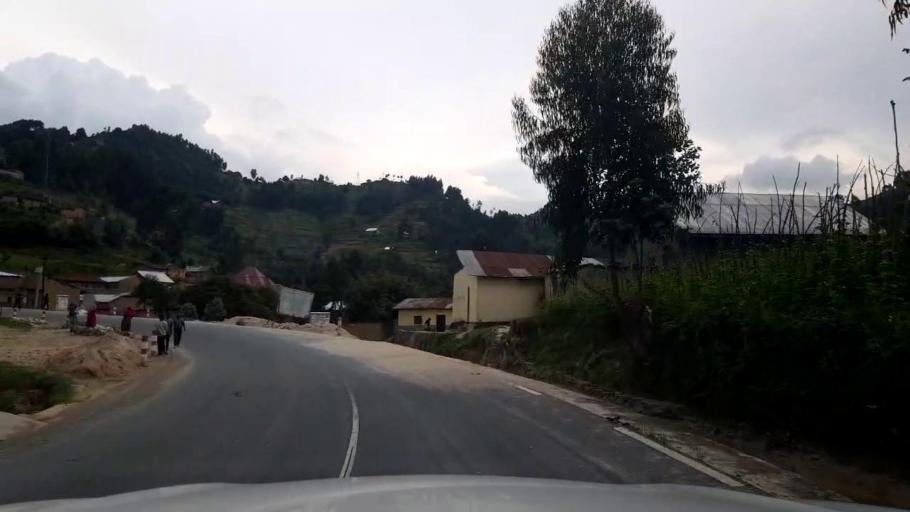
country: RW
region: Northern Province
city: Musanze
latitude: -1.6862
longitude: 29.5164
